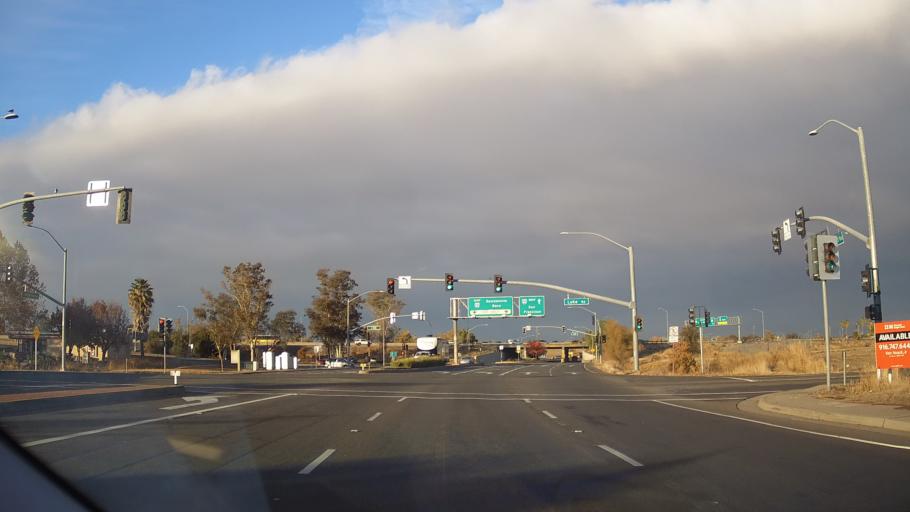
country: US
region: California
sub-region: Yolo County
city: West Sacramento
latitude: 38.5719
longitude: -121.5783
